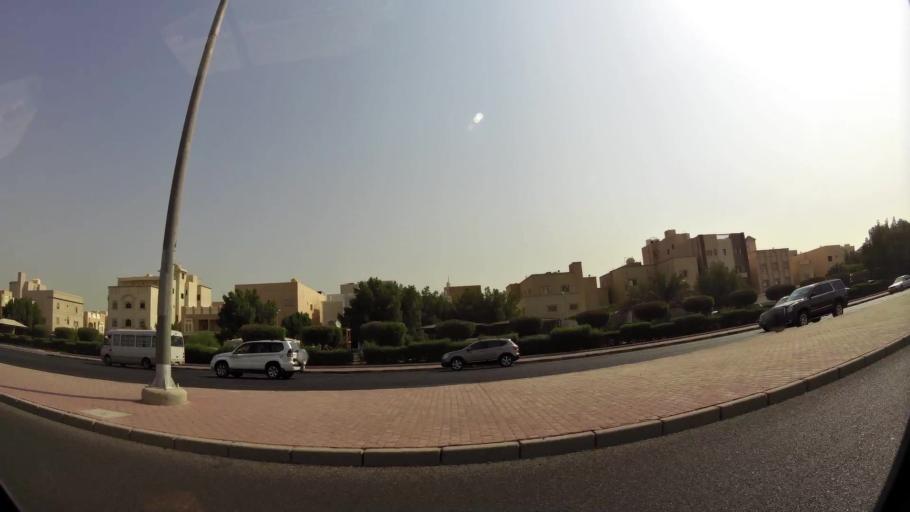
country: KW
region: Al Asimah
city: Ar Rabiyah
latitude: 29.2868
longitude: 47.9280
